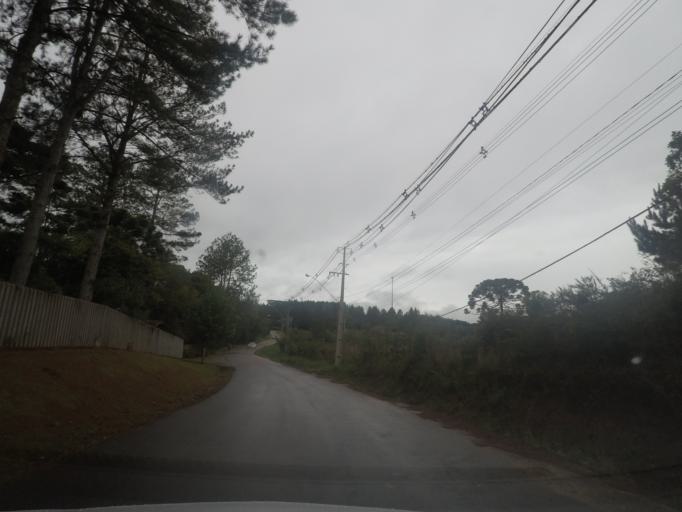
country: BR
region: Parana
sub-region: Campina Grande Do Sul
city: Campina Grande do Sul
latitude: -25.3140
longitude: -49.0763
